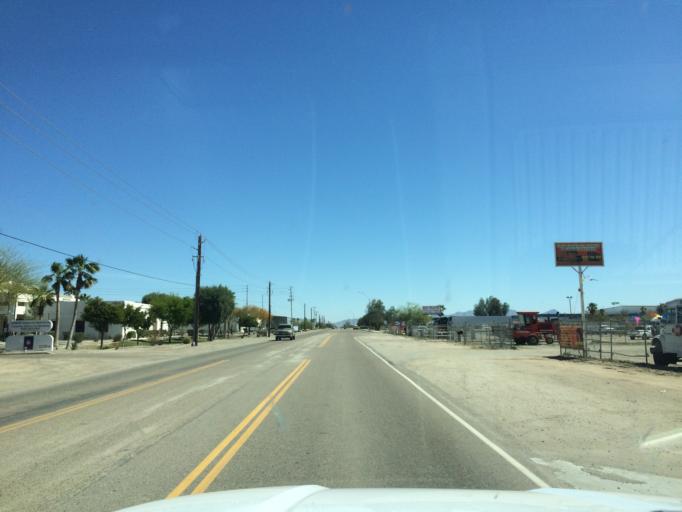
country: US
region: Arizona
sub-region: Yuma County
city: Yuma
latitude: 32.6551
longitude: -114.5786
